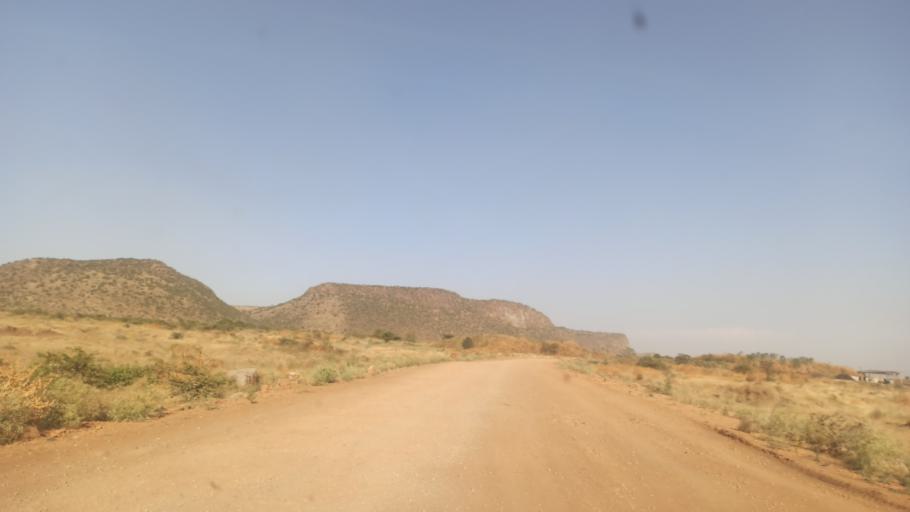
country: ET
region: Oromiya
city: Ziway
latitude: 7.9355
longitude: 38.6180
